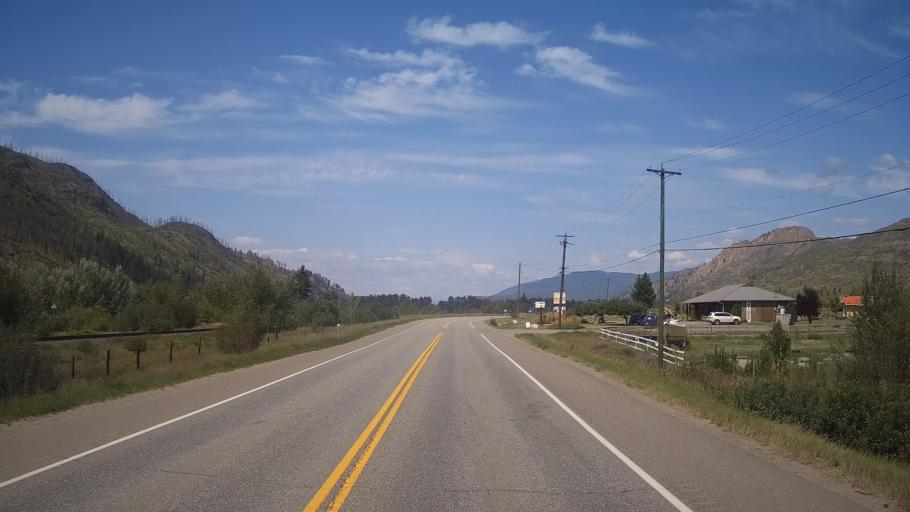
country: CA
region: British Columbia
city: Kamloops
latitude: 51.1361
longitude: -120.1242
